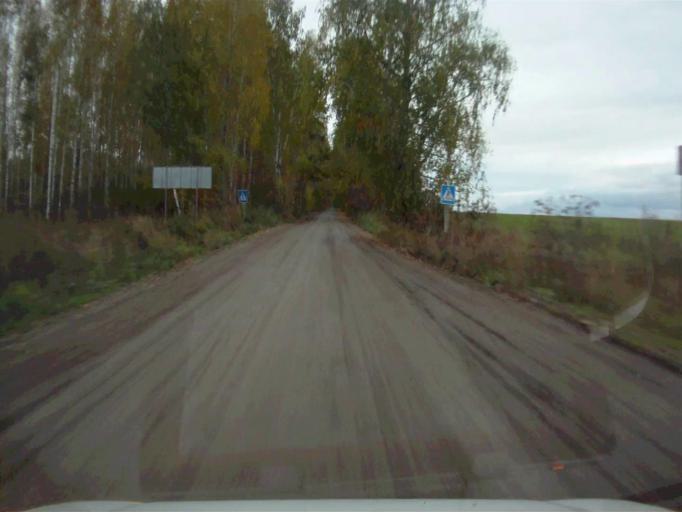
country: RU
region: Sverdlovsk
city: Mikhaylovsk
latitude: 56.1697
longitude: 59.2257
